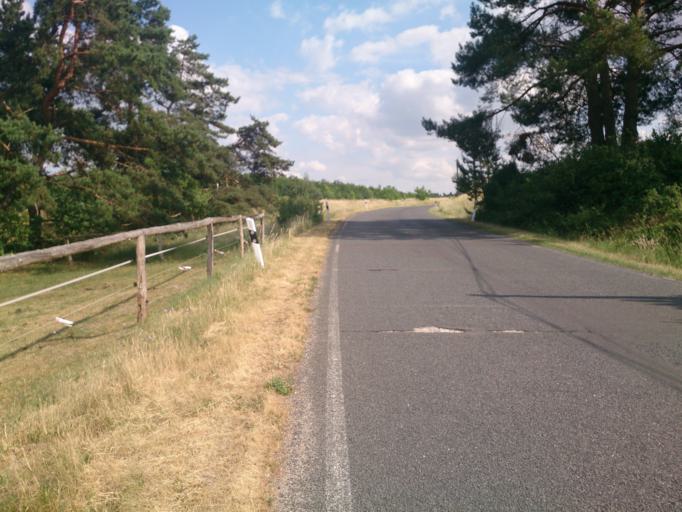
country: DE
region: Mecklenburg-Vorpommern
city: Plau am See
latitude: 53.4287
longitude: 12.3227
